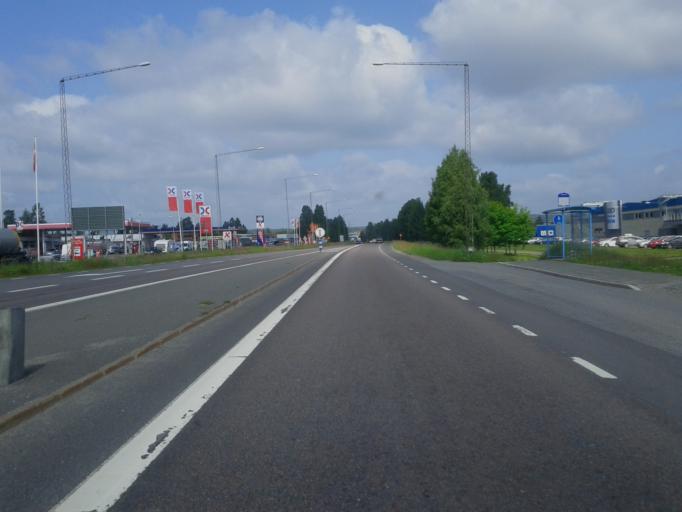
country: SE
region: Vaesterbotten
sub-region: Skelleftea Kommun
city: Skelleftea
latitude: 64.7374
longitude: 20.9659
